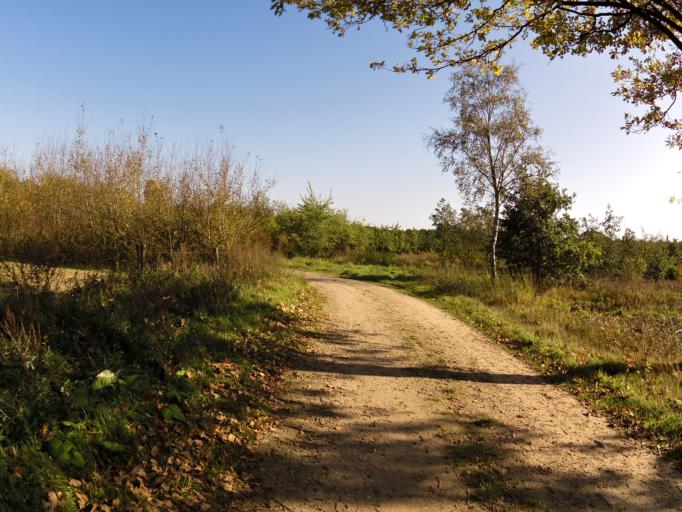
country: NL
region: Limburg
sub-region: Gemeente Weert
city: Weert
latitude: 51.2845
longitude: 5.6552
